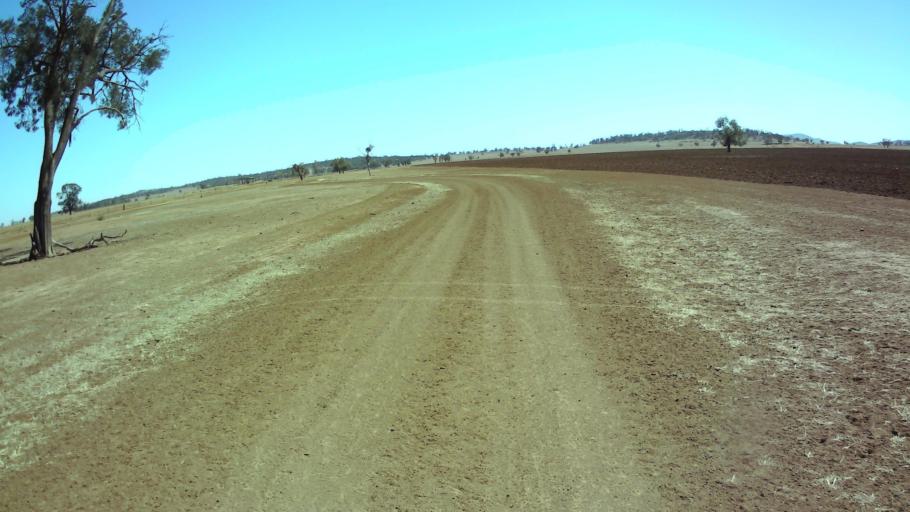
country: AU
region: New South Wales
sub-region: Forbes
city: Forbes
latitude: -33.7102
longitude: 147.6677
